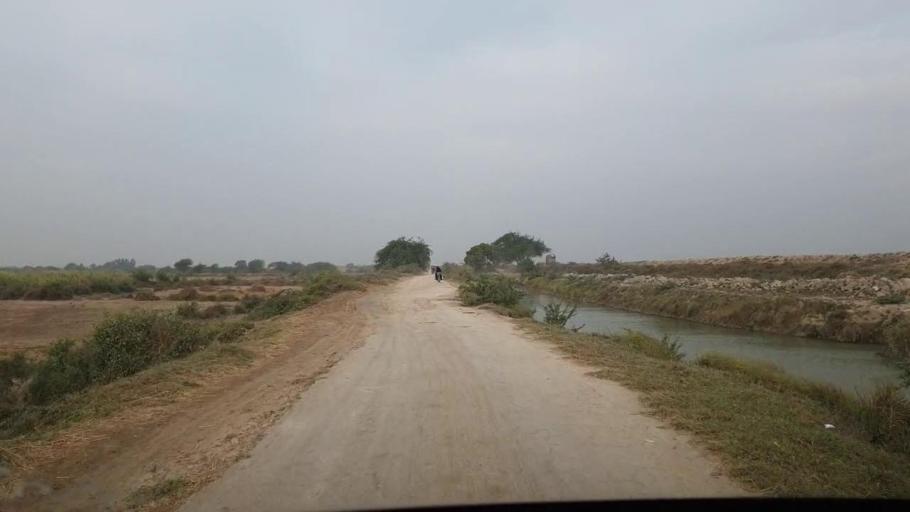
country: PK
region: Sindh
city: Chuhar Jamali
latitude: 24.4045
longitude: 67.9585
